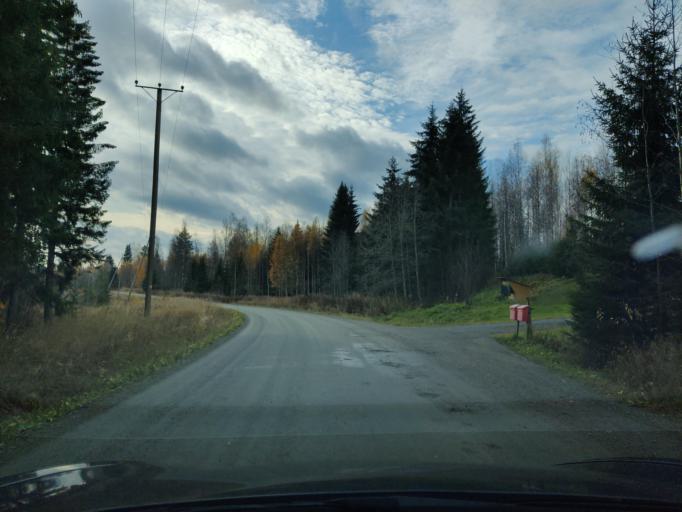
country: FI
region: Northern Savo
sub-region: Kuopio
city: Siilinjaervi
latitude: 63.1177
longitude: 27.5444
